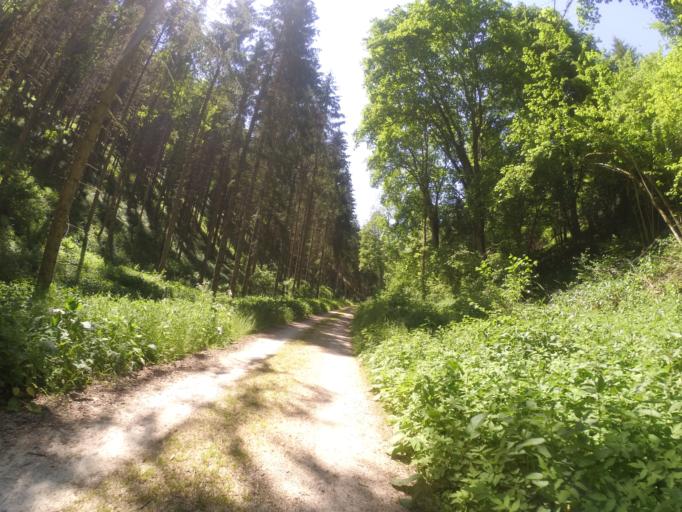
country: DE
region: Baden-Wuerttemberg
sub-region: Tuebingen Region
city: Blaubeuren
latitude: 48.4524
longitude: 9.8417
